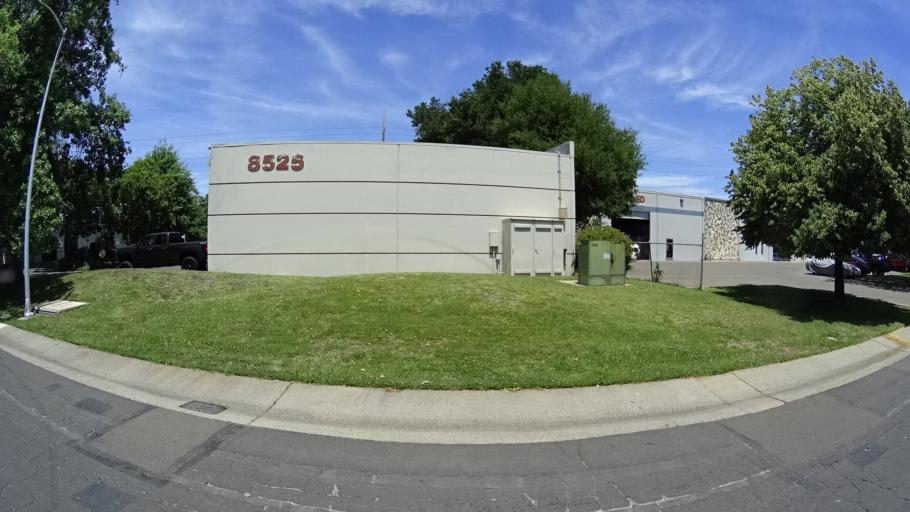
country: US
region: California
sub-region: Sacramento County
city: Rosemont
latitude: 38.5317
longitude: -121.3890
